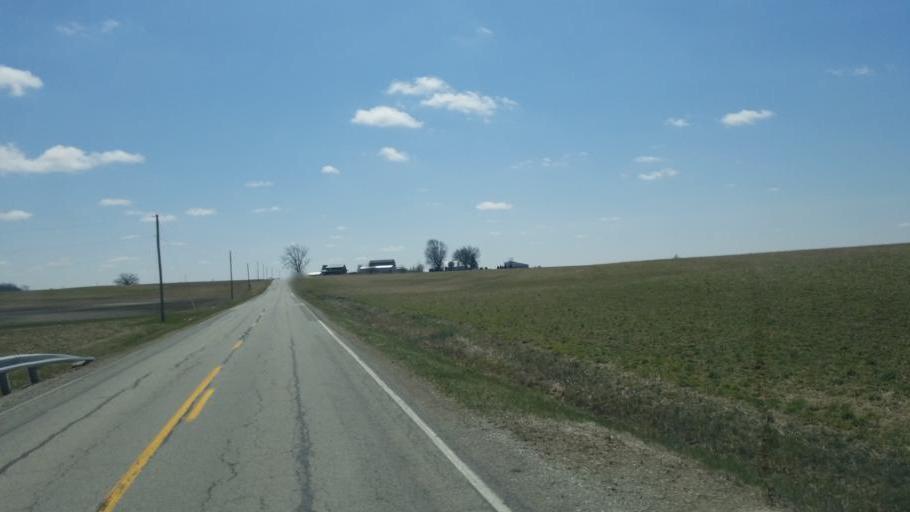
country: US
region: Ohio
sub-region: Marion County
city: Marion
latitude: 40.6779
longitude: -83.2344
